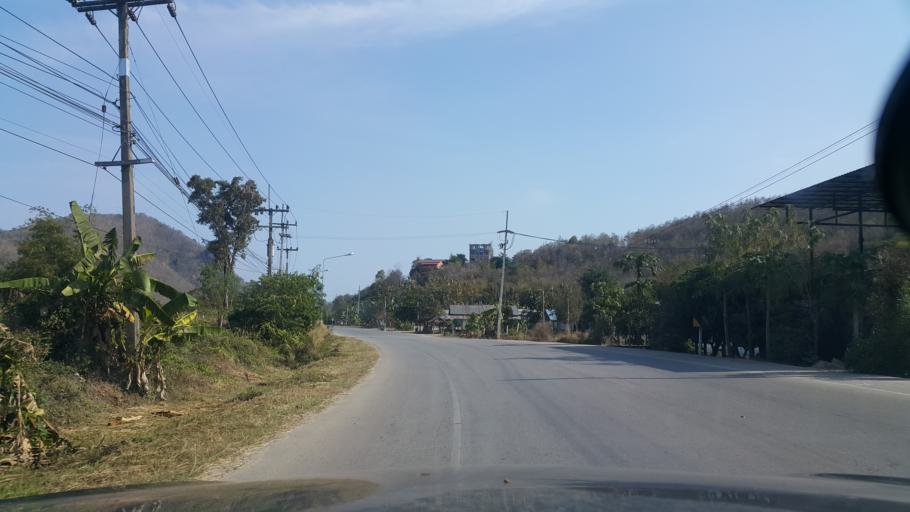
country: LA
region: Vientiane
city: Muang Sanakham
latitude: 17.8990
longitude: 101.7176
